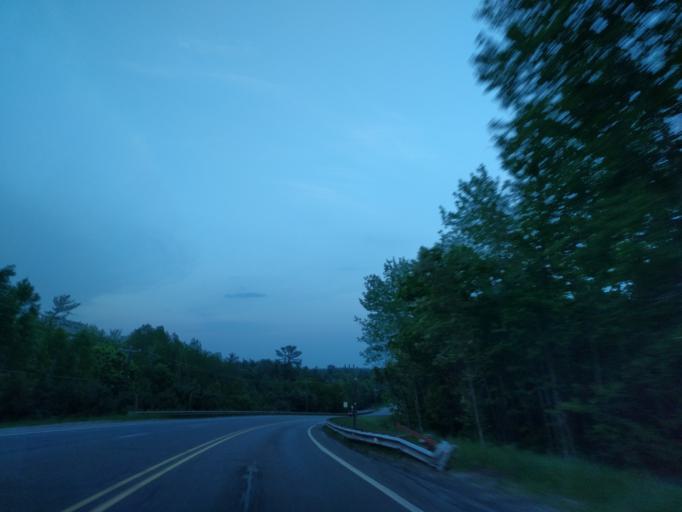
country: US
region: Michigan
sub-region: Marquette County
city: Trowbridge Park
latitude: 46.5645
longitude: -87.4481
